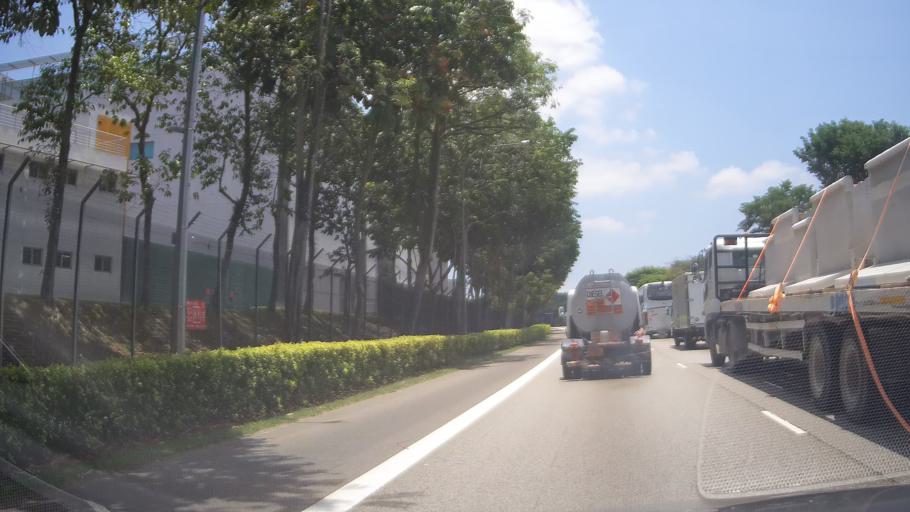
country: MY
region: Johor
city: Johor Bahru
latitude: 1.3701
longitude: 103.7205
